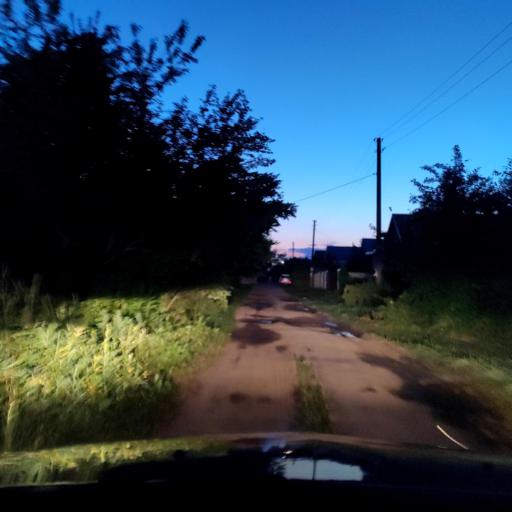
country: RU
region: Voronezj
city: Podgornoye
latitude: 51.8016
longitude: 39.2265
